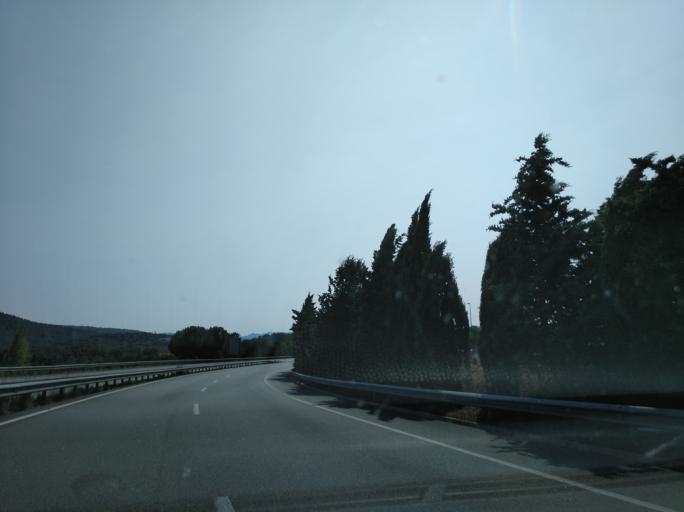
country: ES
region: Catalonia
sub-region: Provincia de Barcelona
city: La Roca del Valles
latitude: 41.6001
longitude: 2.3360
